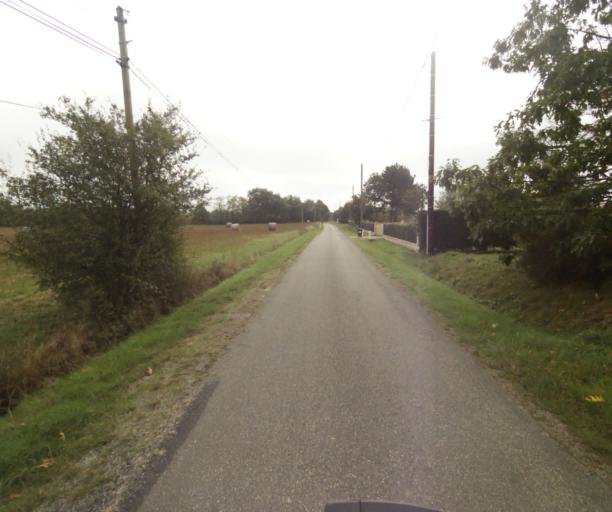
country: FR
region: Midi-Pyrenees
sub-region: Departement du Tarn-et-Garonne
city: Campsas
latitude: 43.8840
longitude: 1.3488
